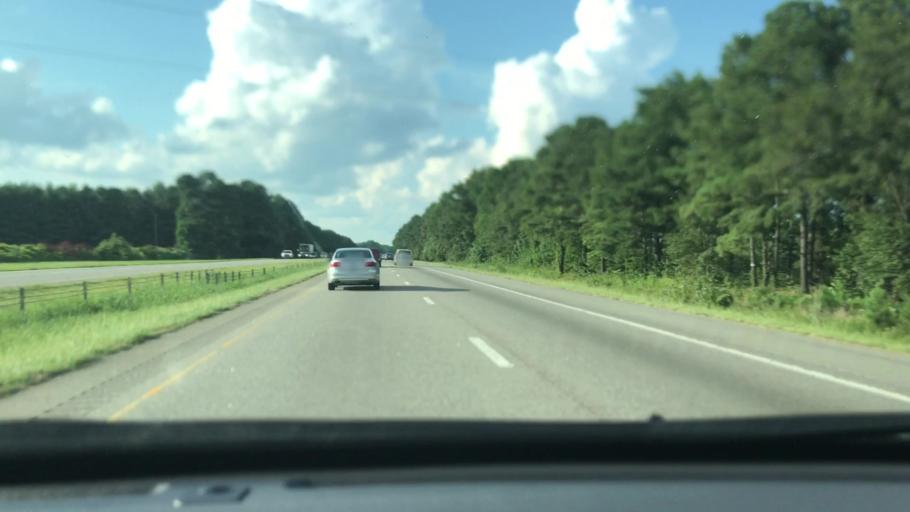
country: US
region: North Carolina
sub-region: Robeson County
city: Saint Pauls
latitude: 34.7540
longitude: -78.9970
